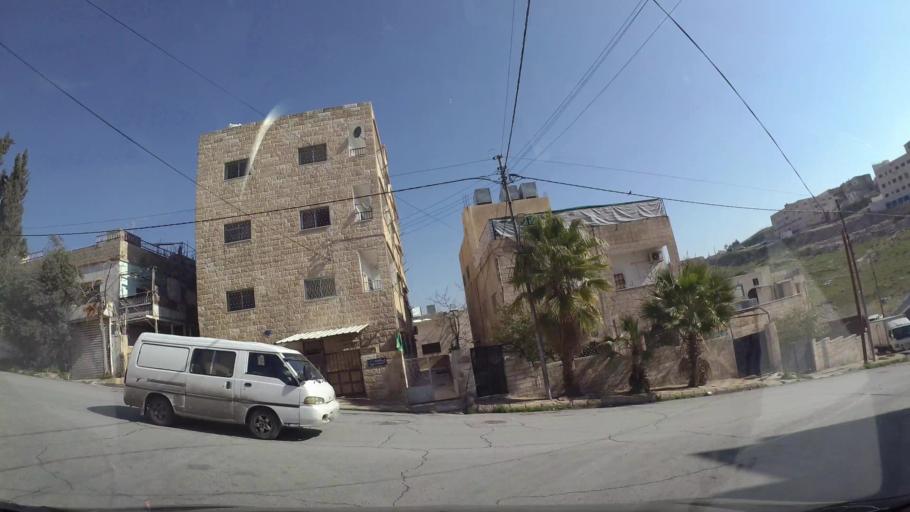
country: JO
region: Amman
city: Amman
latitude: 31.9901
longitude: 35.9924
